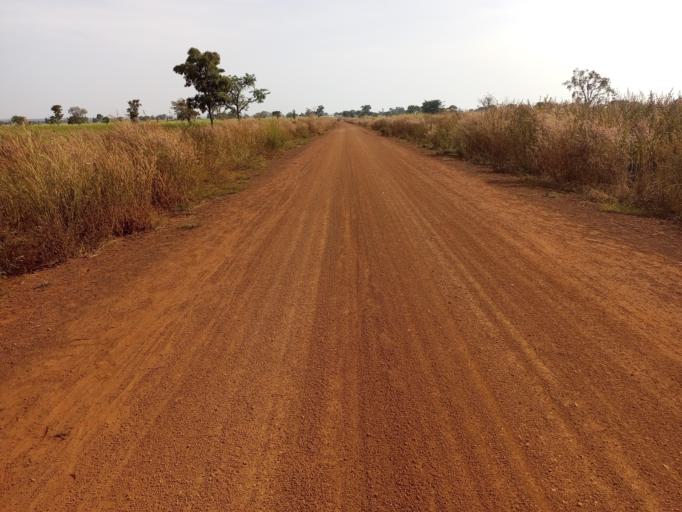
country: TG
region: Kara
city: Kande
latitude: 10.0970
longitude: 0.7505
